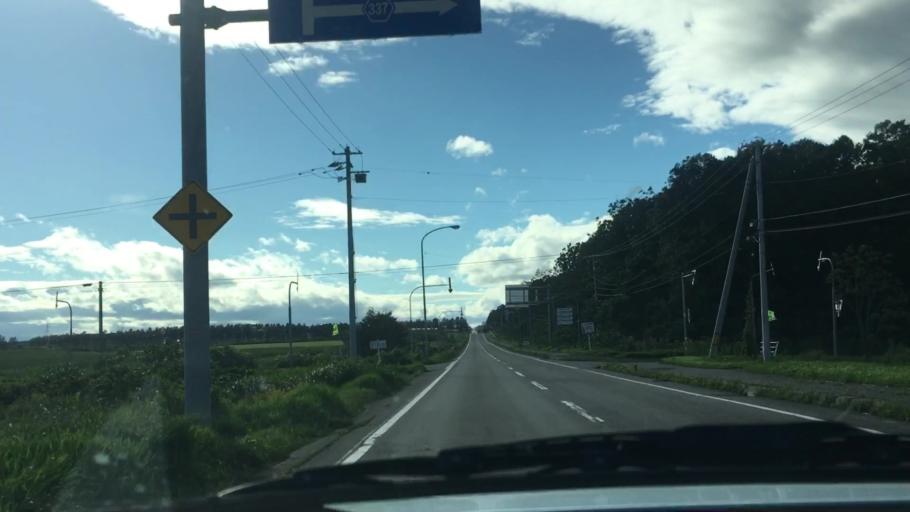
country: JP
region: Hokkaido
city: Otofuke
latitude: 43.1554
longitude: 143.1909
